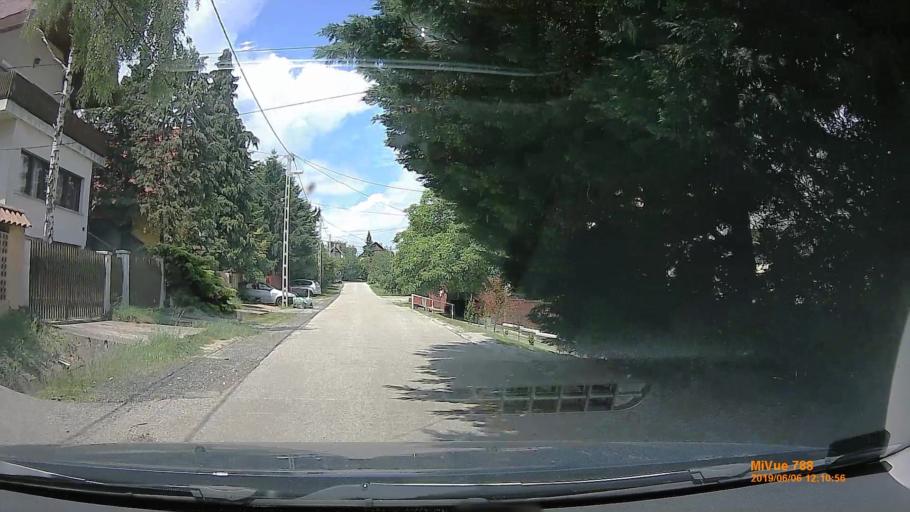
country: HU
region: Pest
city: Kerepes
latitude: 47.5714
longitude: 19.2625
